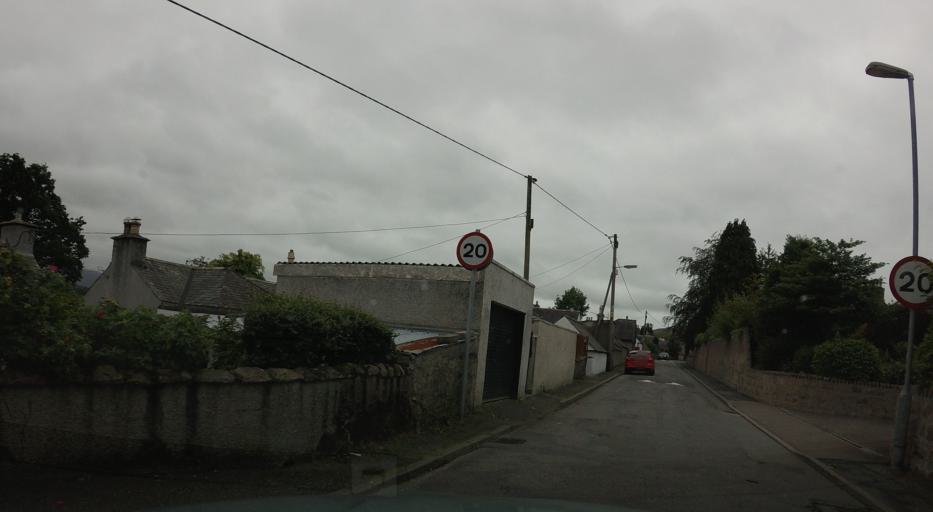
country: GB
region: Scotland
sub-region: Aberdeenshire
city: Banchory
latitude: 57.0522
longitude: -2.4938
